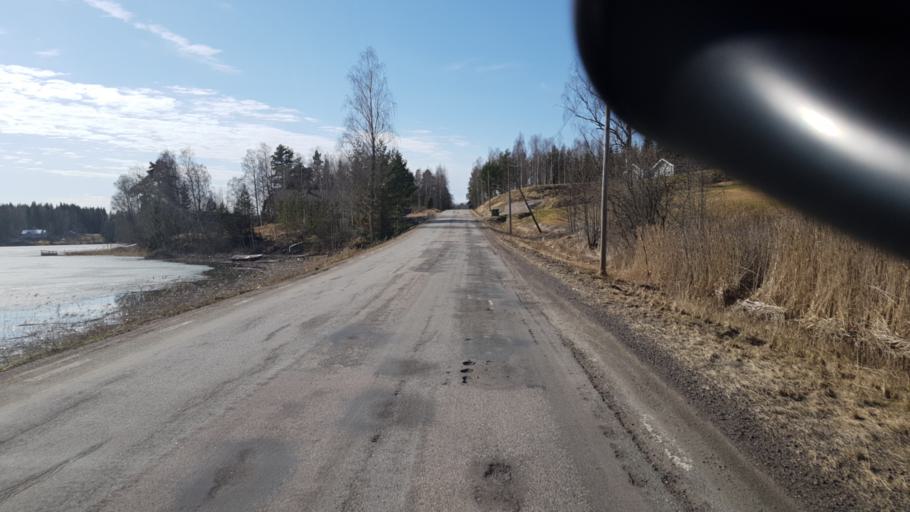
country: SE
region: Vaermland
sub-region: Arvika Kommun
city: Arvika
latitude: 59.6633
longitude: 12.6937
